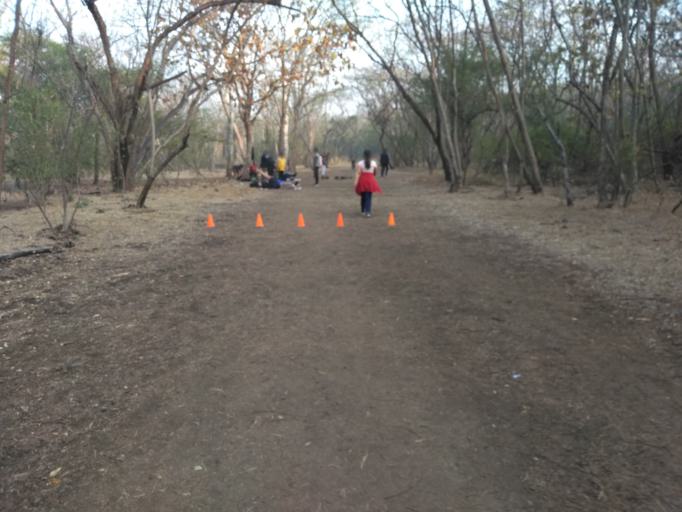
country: IN
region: Maharashtra
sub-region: Pune Division
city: Pune
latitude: 18.4751
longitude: 73.8425
